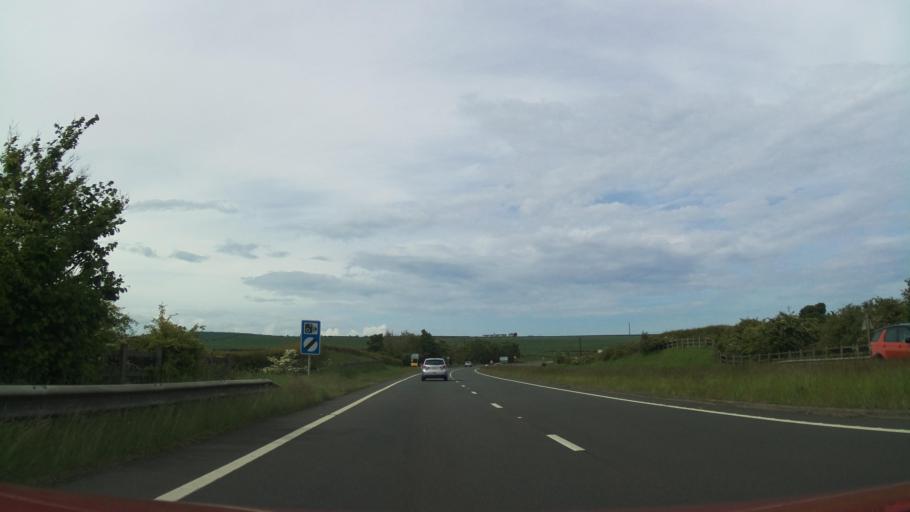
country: GB
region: England
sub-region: Northumberland
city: Berwick-Upon-Tweed
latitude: 55.7685
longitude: -2.0442
